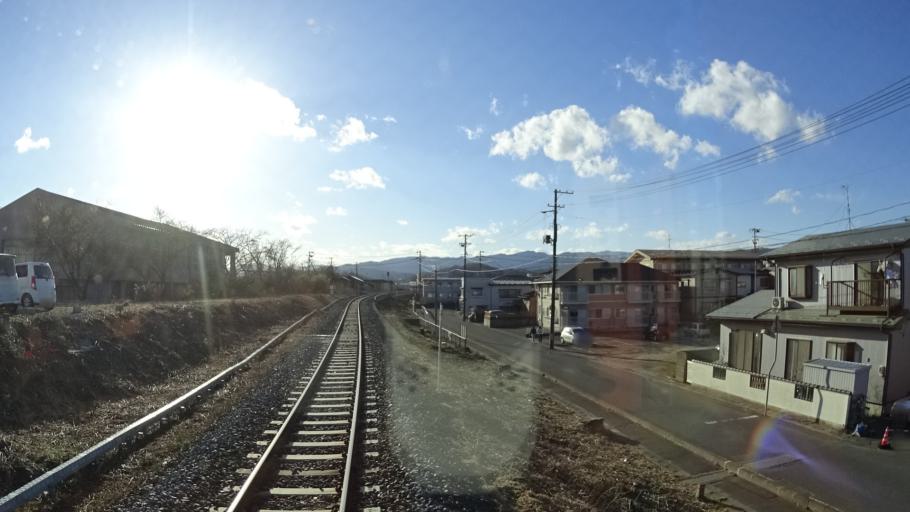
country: JP
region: Iwate
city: Miyako
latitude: 39.6371
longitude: 141.9582
